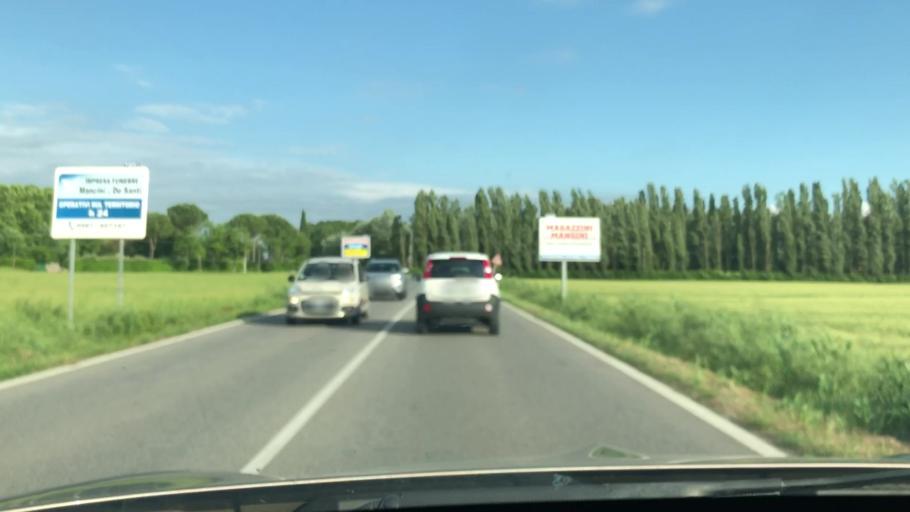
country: IT
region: Tuscany
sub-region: Province of Pisa
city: Treggiaia
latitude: 43.6163
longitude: 10.6773
